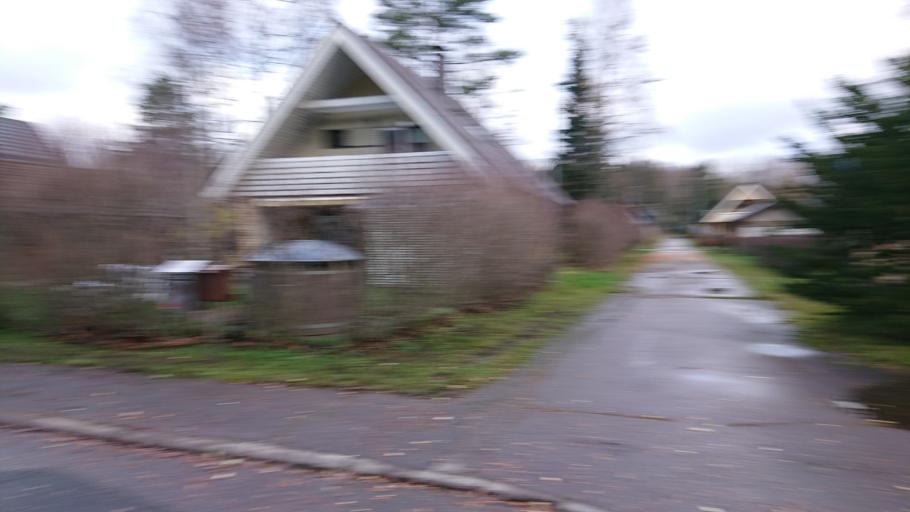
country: FI
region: Pirkanmaa
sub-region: Tampere
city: Tampere
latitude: 61.4384
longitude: 23.8517
